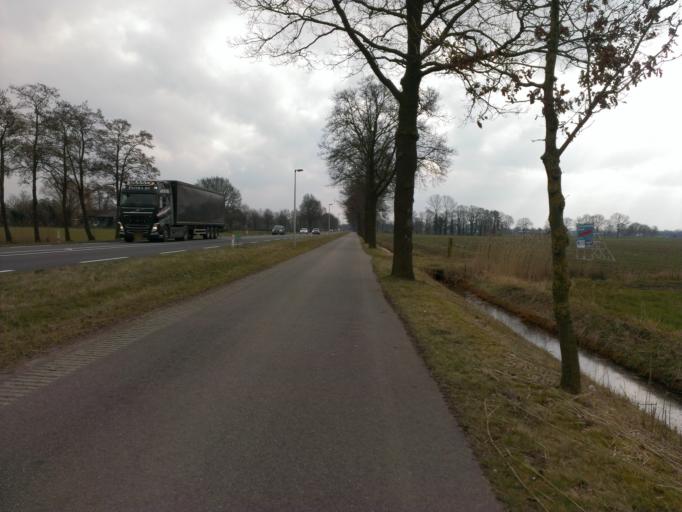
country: NL
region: Overijssel
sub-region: Gemeente Borne
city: Borne
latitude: 52.3183
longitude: 6.7309
